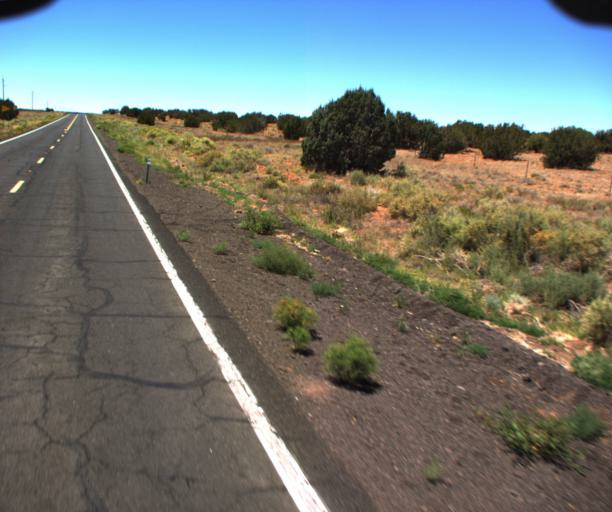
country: US
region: Arizona
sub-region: Coconino County
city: LeChee
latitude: 34.8542
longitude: -110.9231
